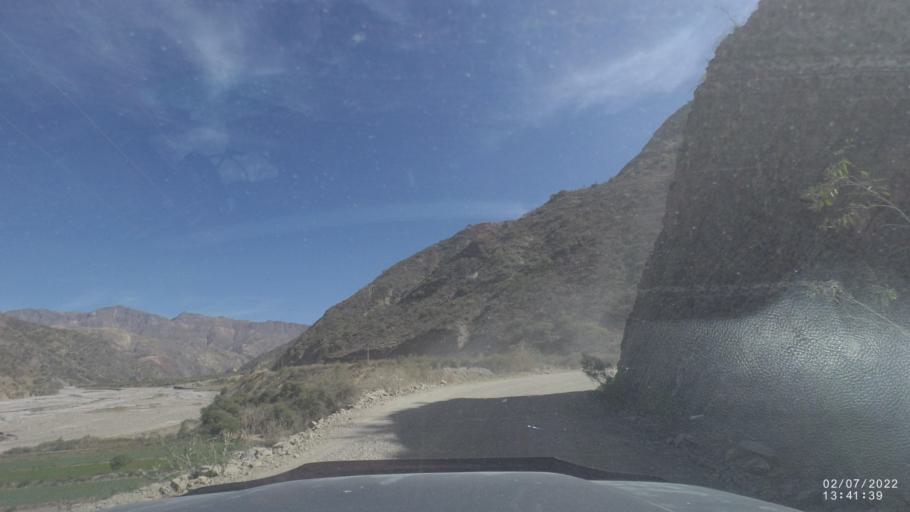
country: BO
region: Cochabamba
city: Irpa Irpa
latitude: -17.7983
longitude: -66.3529
